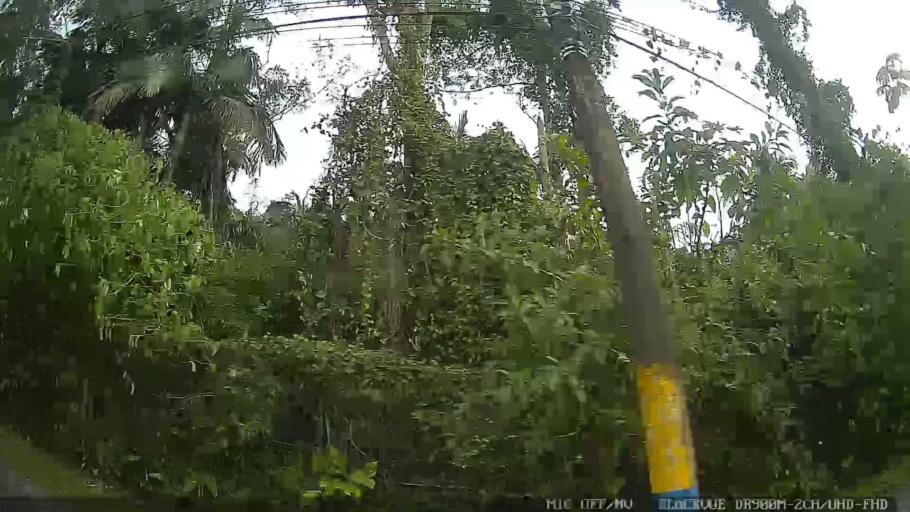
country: BR
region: Sao Paulo
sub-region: Cubatao
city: Cubatao
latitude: -23.8753
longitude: -46.4265
